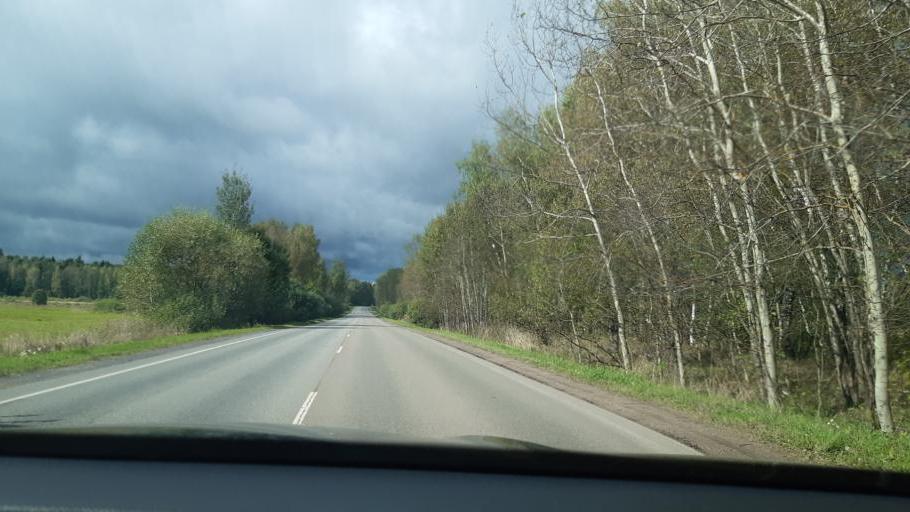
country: RU
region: Moskovskaya
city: Melikhovo
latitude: 55.1162
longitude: 37.6392
